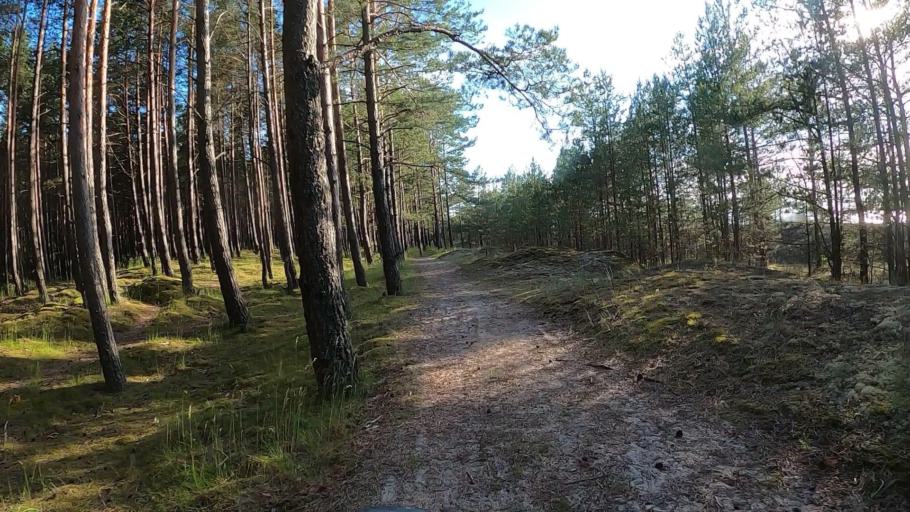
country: LV
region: Carnikava
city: Carnikava
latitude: 57.1208
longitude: 24.2053
